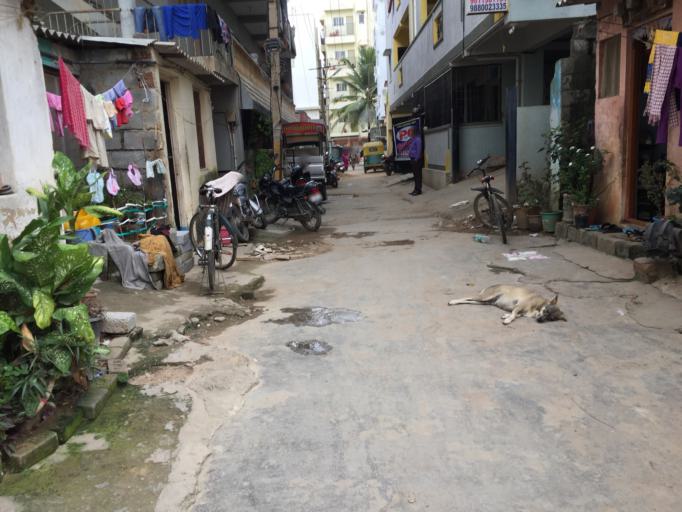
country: IN
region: Karnataka
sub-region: Bangalore Urban
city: Bangalore
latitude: 12.9552
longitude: 77.6547
